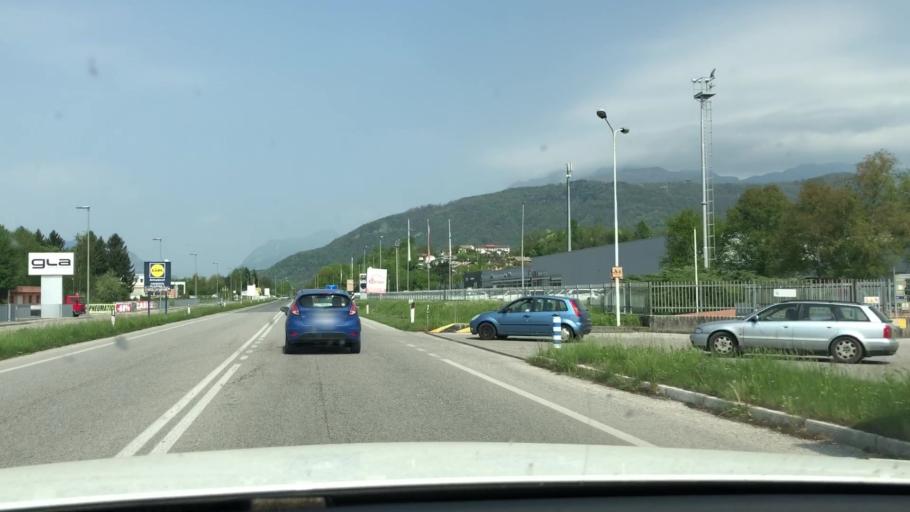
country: IT
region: Friuli Venezia Giulia
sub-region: Provincia di Udine
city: Magnano in Riviera
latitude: 46.2061
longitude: 13.1881
